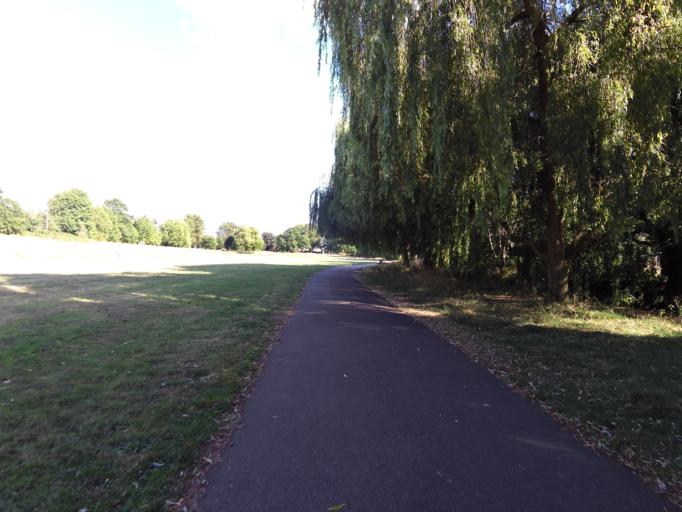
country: GB
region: England
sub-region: Greater London
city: Wood Green
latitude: 51.6176
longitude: -0.1284
